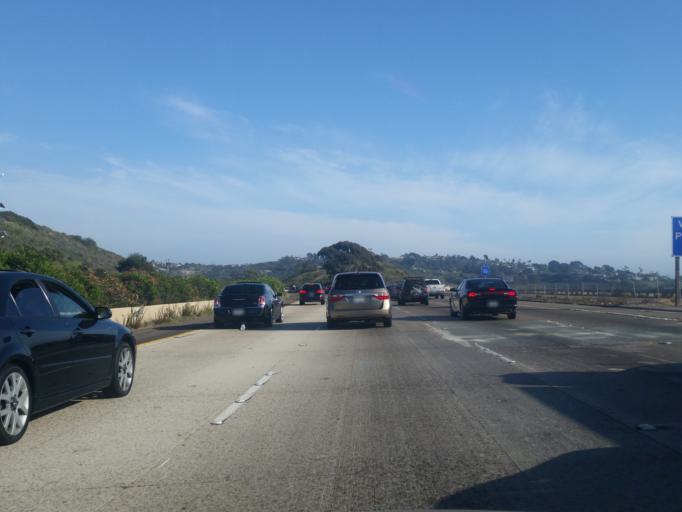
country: US
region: California
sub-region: San Diego County
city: Solana Beach
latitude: 33.0174
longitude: -117.2720
